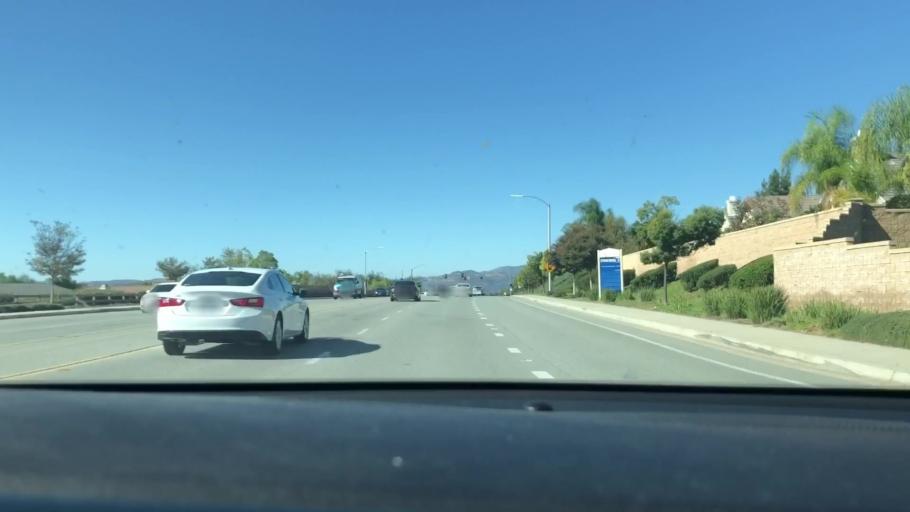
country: US
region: California
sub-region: Riverside County
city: Murrieta Hot Springs
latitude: 33.5970
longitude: -117.1840
